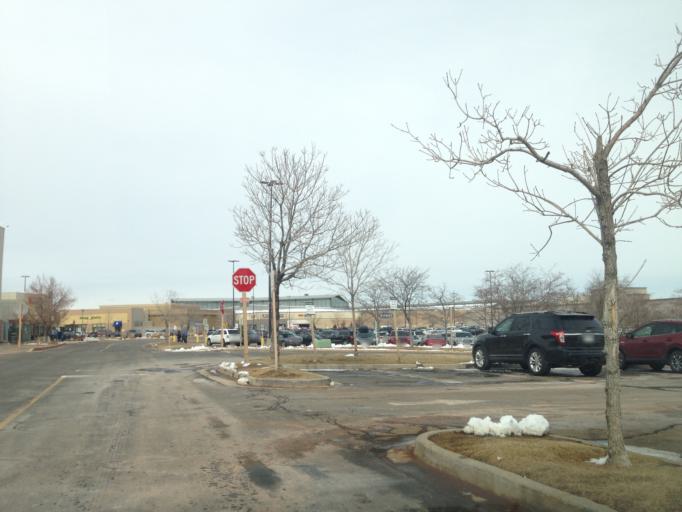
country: US
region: Colorado
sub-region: Boulder County
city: Superior
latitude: 39.9299
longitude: -105.1342
